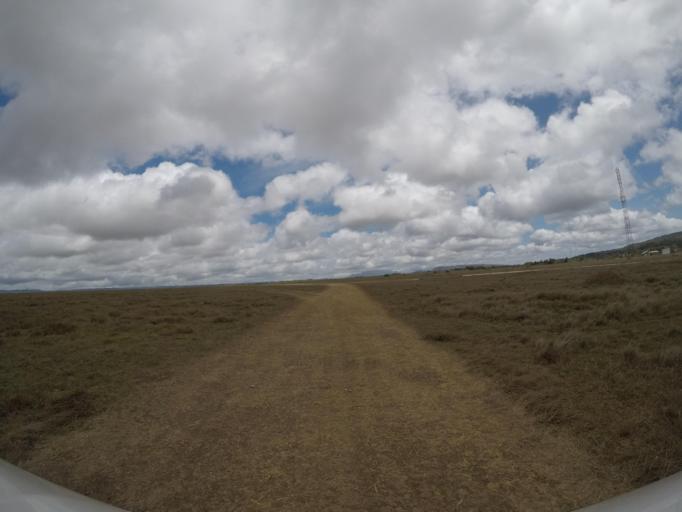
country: TL
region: Lautem
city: Lospalos
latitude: -8.4436
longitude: 126.9897
